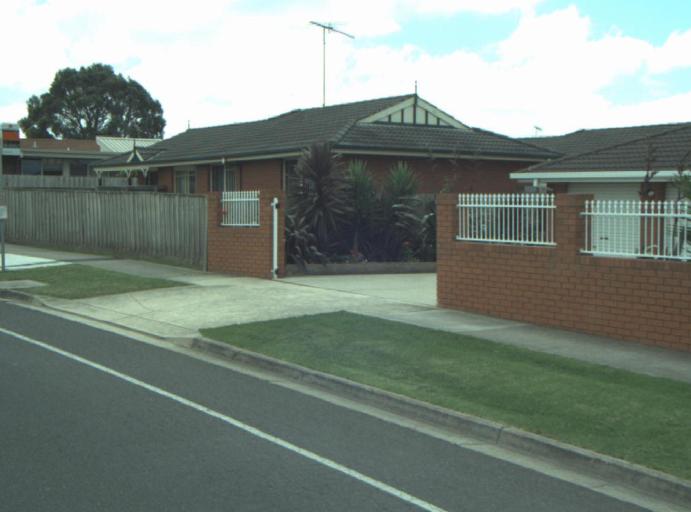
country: AU
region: Victoria
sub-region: Greater Geelong
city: Wandana Heights
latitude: -38.1890
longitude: 144.3202
